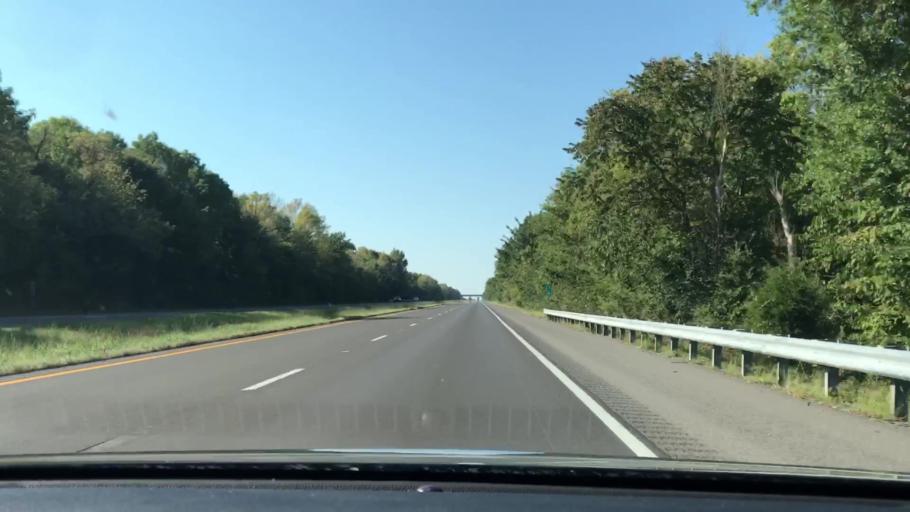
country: US
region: Kentucky
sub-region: Graves County
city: Mayfield
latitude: 36.6768
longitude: -88.7351
